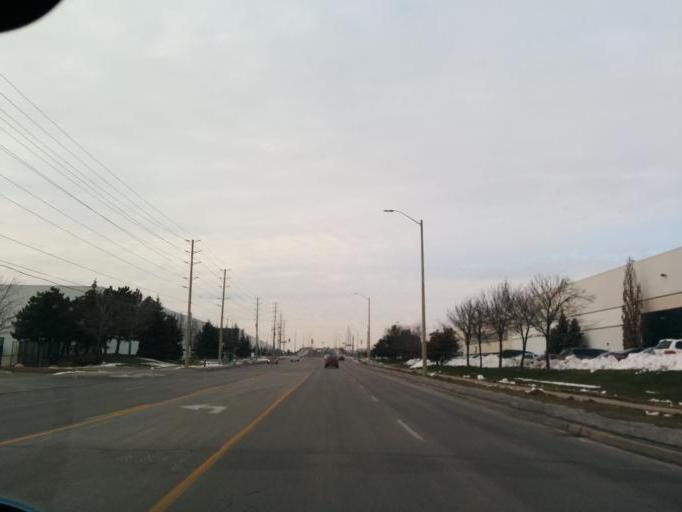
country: CA
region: Ontario
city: Mississauga
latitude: 43.6198
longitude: -79.6941
